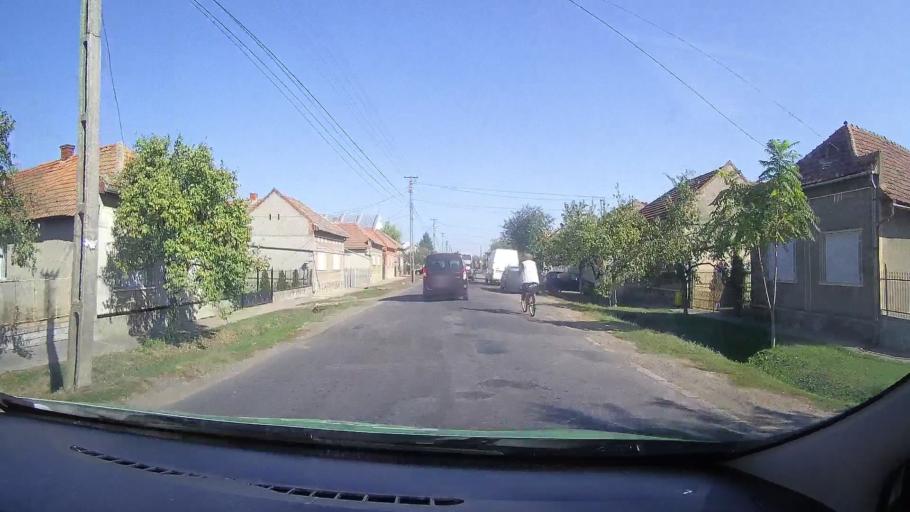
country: RO
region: Satu Mare
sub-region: Comuna Capleni
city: Capleni
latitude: 47.7007
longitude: 22.4904
